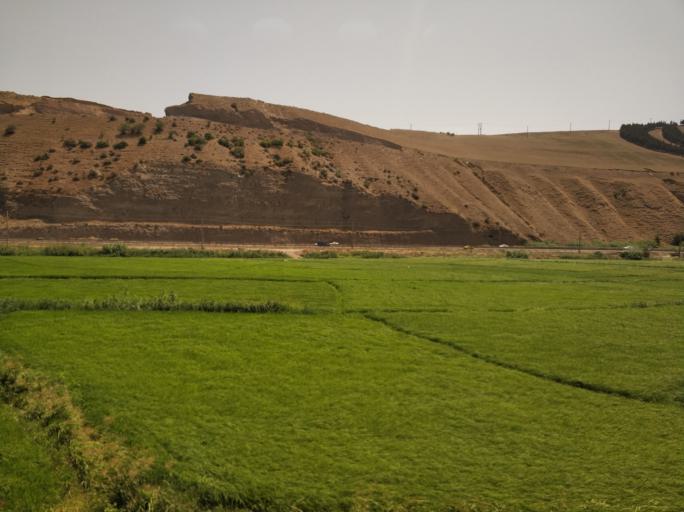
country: IR
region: Gilan
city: Pa'in-e Bazar-e Rudbar
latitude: 36.9179
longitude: 49.5219
